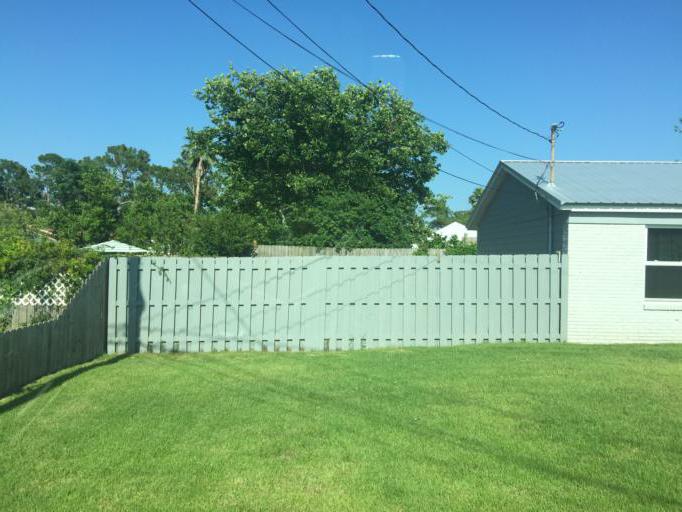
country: US
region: Florida
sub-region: Bay County
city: Panama City Beach
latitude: 30.2015
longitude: -85.8389
